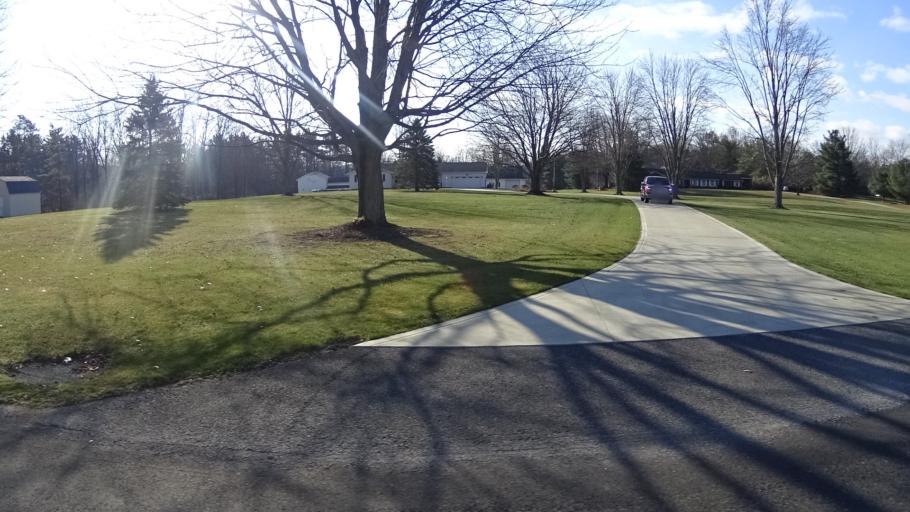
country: US
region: Ohio
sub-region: Lorain County
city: Wellington
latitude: 41.2235
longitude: -82.2256
